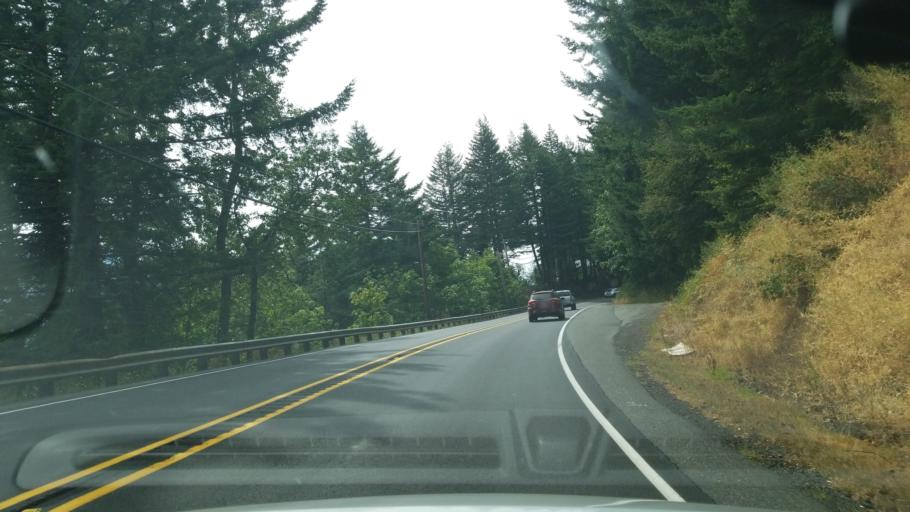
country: US
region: Washington
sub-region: Skamania County
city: Carson
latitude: 45.7073
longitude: -121.8438
